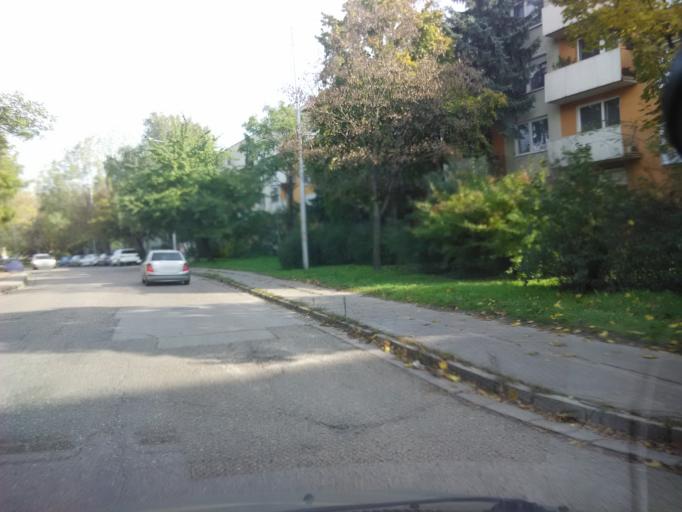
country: SK
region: Nitriansky
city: Komarno
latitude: 47.7643
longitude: 18.1197
